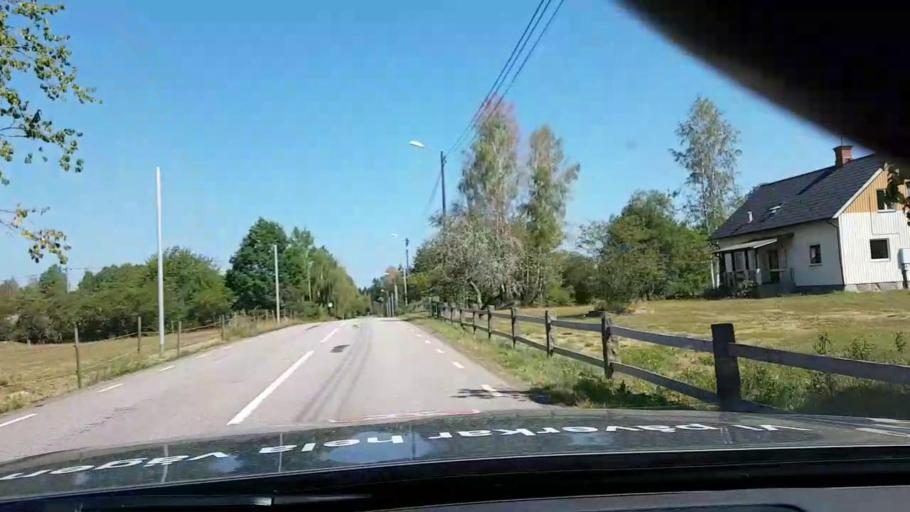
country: SE
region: Kalmar
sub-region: Hultsfreds Kommun
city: Virserum
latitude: 57.1356
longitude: 15.6596
